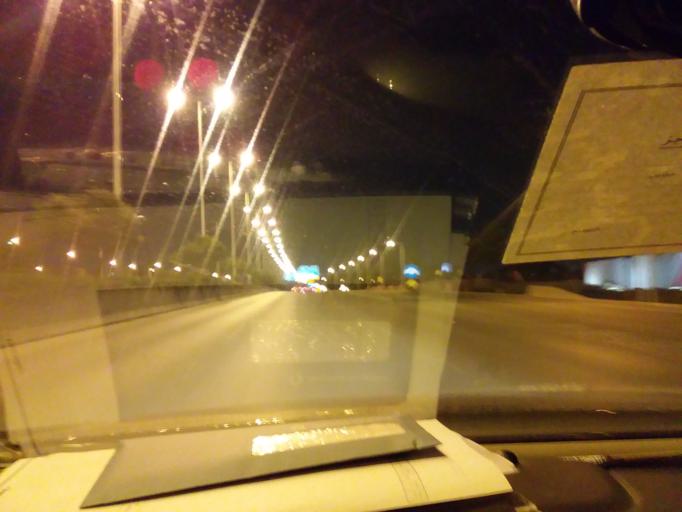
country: SA
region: Ar Riyad
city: Riyadh
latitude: 24.7245
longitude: 46.7025
